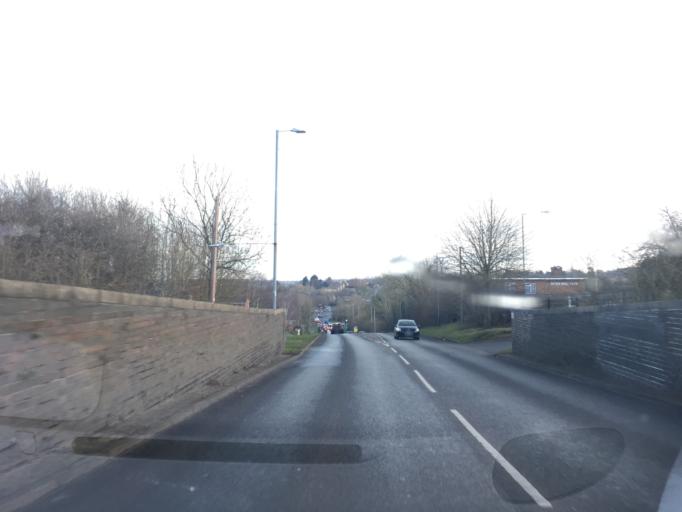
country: GB
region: England
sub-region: Warwickshire
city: Rugby
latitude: 52.3759
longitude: -1.2385
